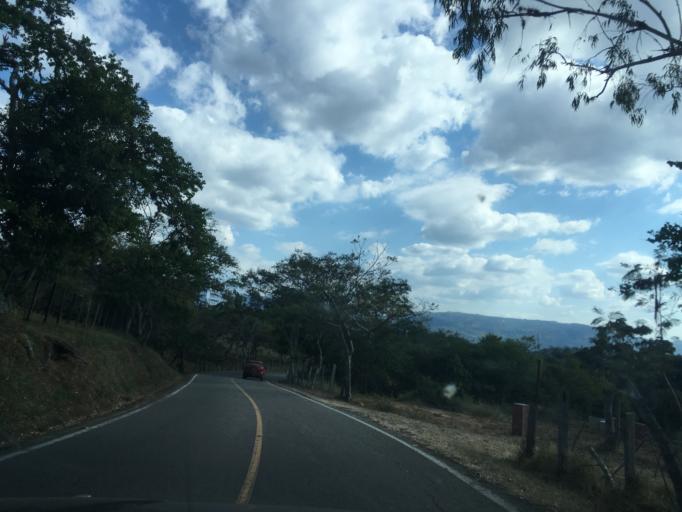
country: CO
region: Santander
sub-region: San Gil
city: San Gil
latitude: 6.5873
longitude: -73.1581
